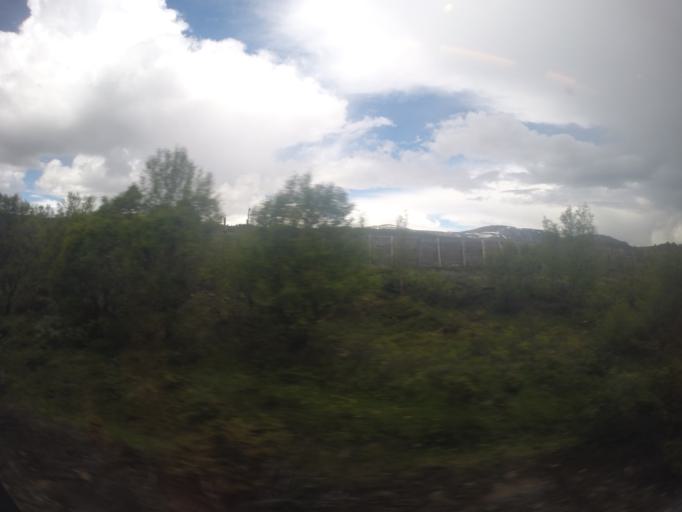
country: NO
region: Sor-Trondelag
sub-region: Oppdal
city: Oppdal
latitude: 62.2748
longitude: 9.5813
